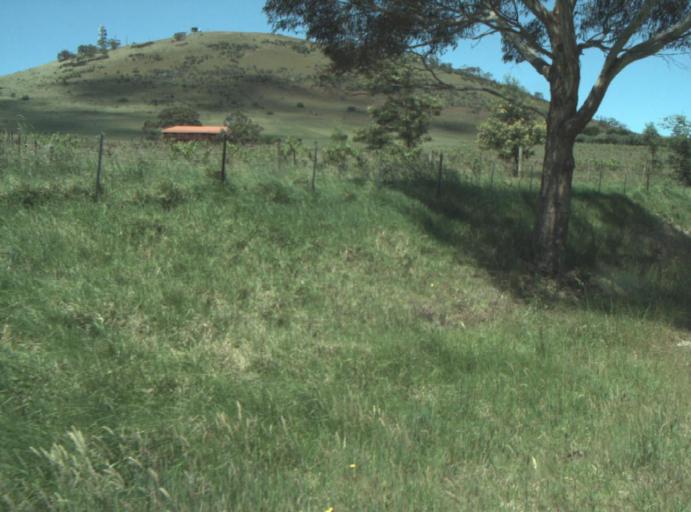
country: AU
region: Victoria
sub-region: Greater Geelong
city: Lara
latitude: -37.8768
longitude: 144.2682
